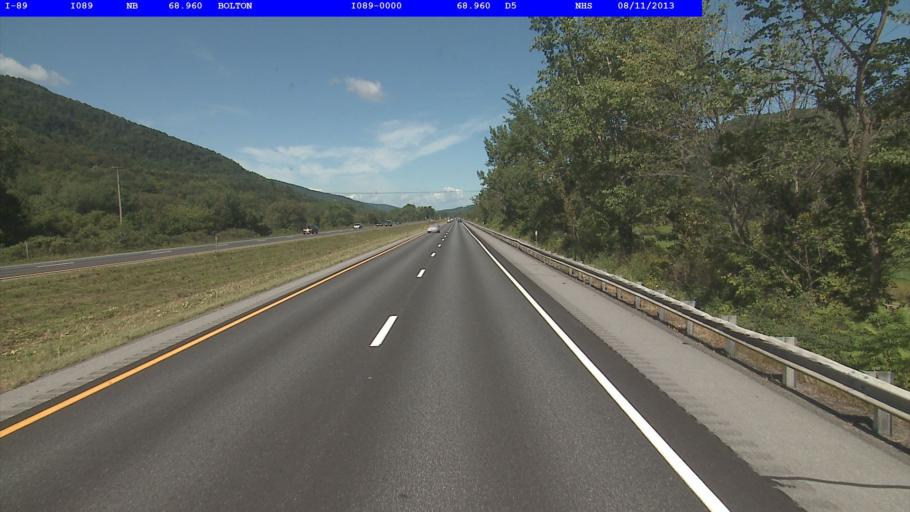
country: US
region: Vermont
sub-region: Washington County
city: Waterbury
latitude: 44.3648
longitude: -72.8484
